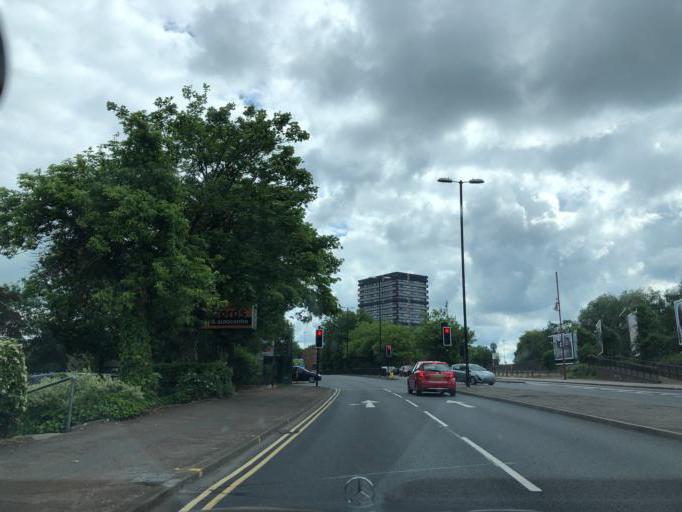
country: GB
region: England
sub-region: Coventry
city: Coventry
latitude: 52.4161
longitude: -1.5092
